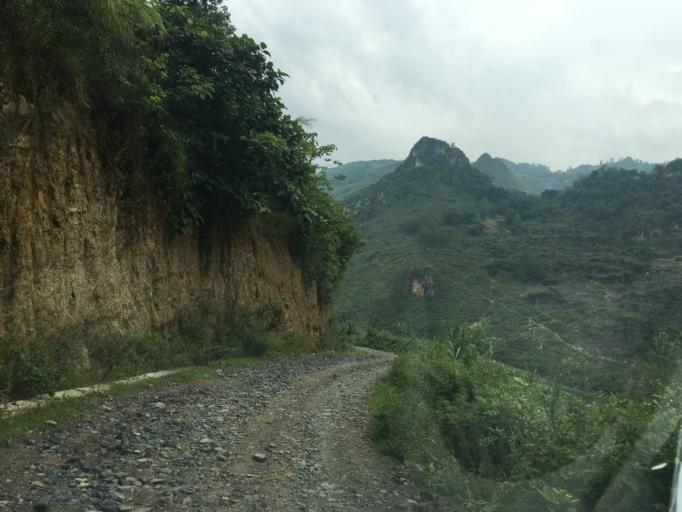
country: CN
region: Guangxi Zhuangzu Zizhiqu
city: Xinzhou
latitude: 25.1776
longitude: 105.7316
